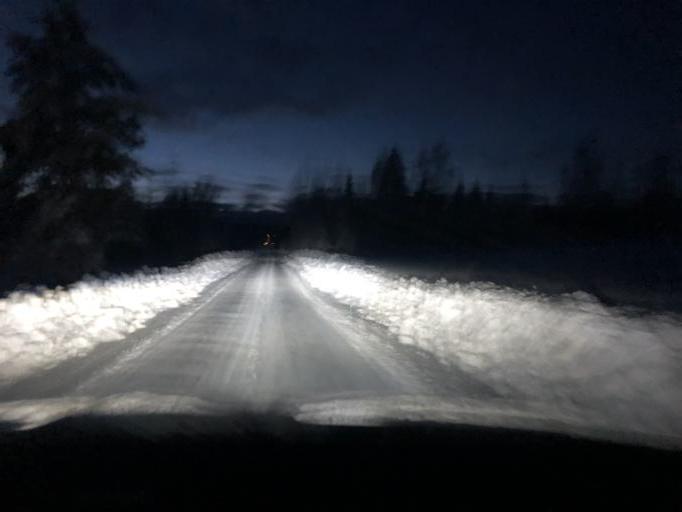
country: SE
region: Vaesternorrland
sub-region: Kramfors Kommun
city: Bollstabruk
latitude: 63.0549
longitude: 17.6709
